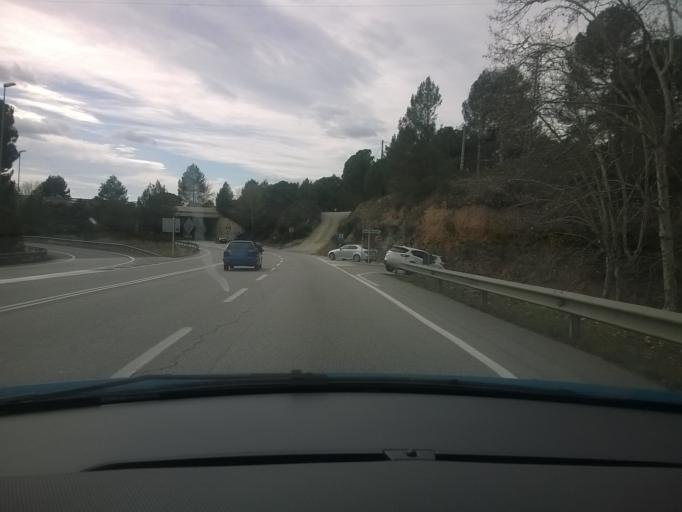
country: ES
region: Catalonia
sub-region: Provincia de Barcelona
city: Rubi
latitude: 41.5110
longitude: 2.0497
